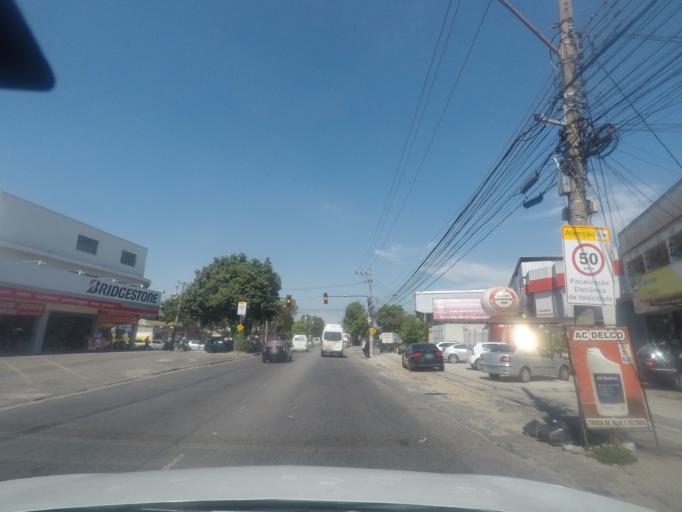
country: BR
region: Rio de Janeiro
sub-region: Nilopolis
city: Nilopolis
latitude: -22.8785
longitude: -43.4491
